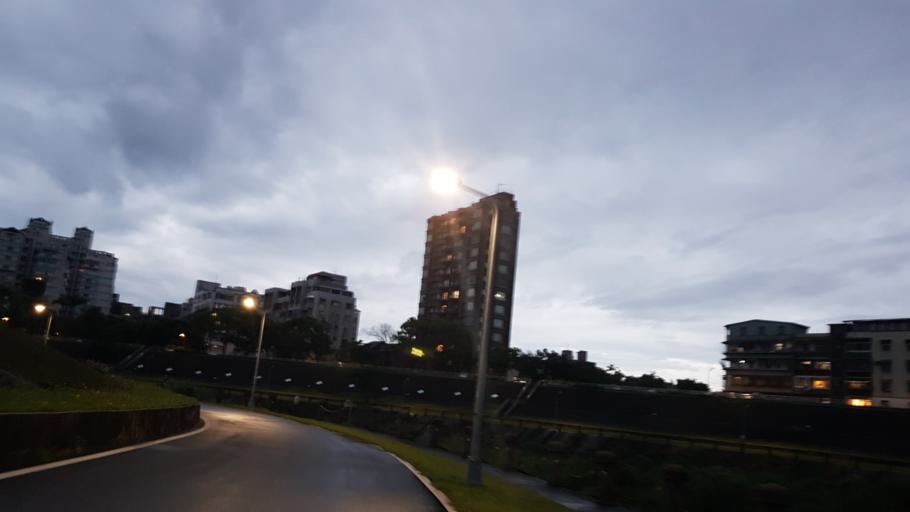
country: TW
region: Taipei
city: Taipei
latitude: 24.9796
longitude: 121.5592
